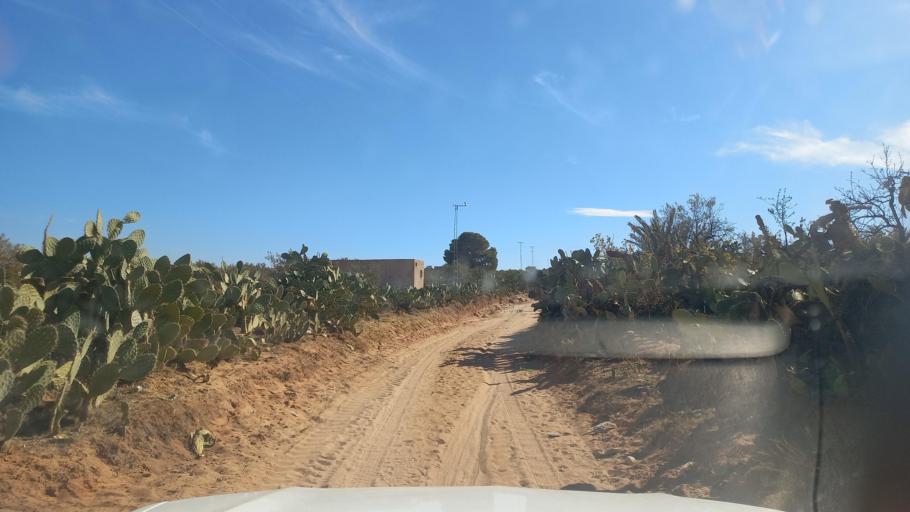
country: TN
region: Al Qasrayn
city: Kasserine
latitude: 35.2088
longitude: 8.9729
